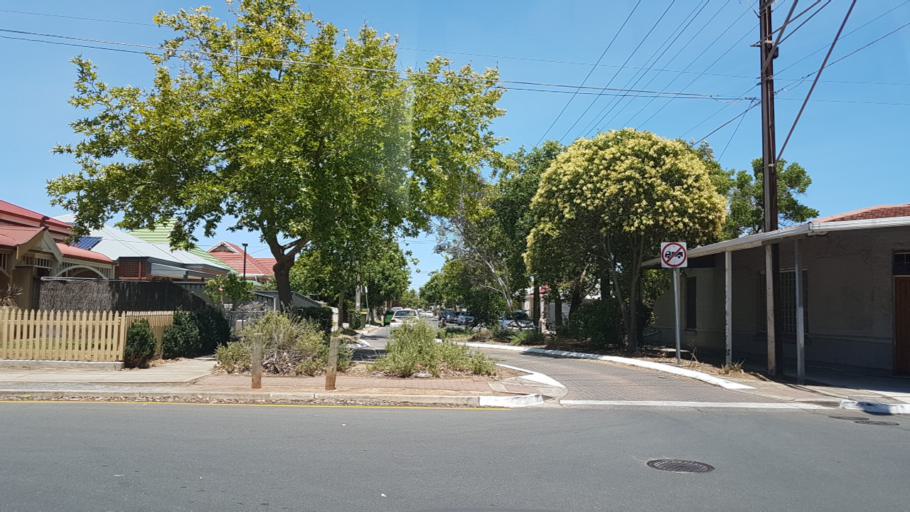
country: AU
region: South Australia
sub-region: City of West Torrens
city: Thebarton
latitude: -34.9182
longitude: 138.5620
